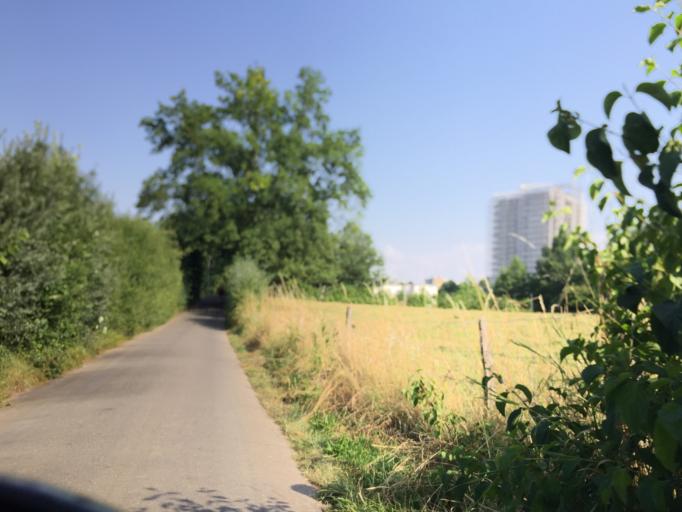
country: CH
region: Bern
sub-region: Bern-Mittelland District
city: Muri
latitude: 46.9418
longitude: 7.4834
